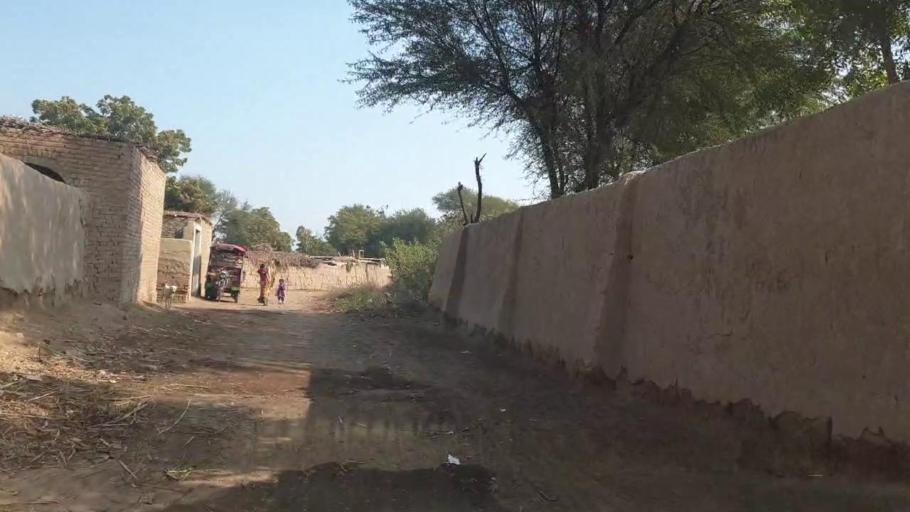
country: PK
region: Sindh
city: Tando Allahyar
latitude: 25.5594
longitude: 68.7570
